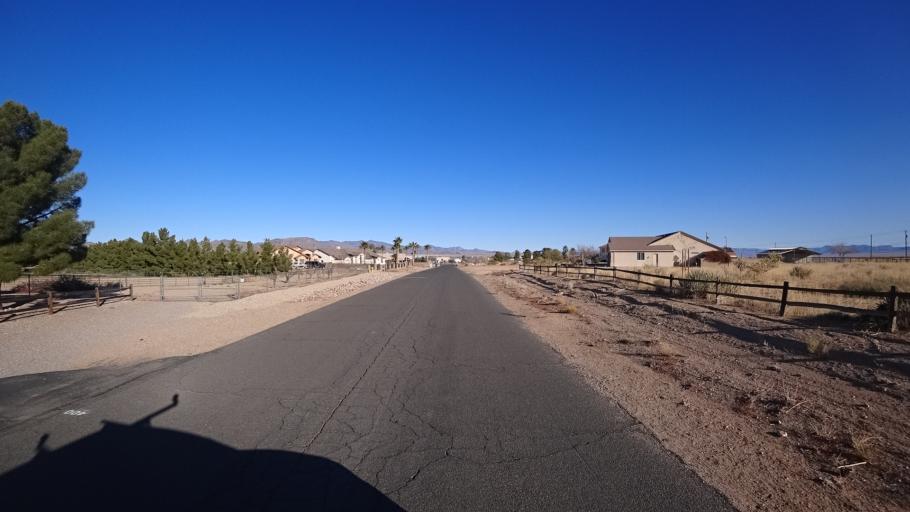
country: US
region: Arizona
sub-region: Mohave County
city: Kingman
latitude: 35.2045
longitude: -113.9952
